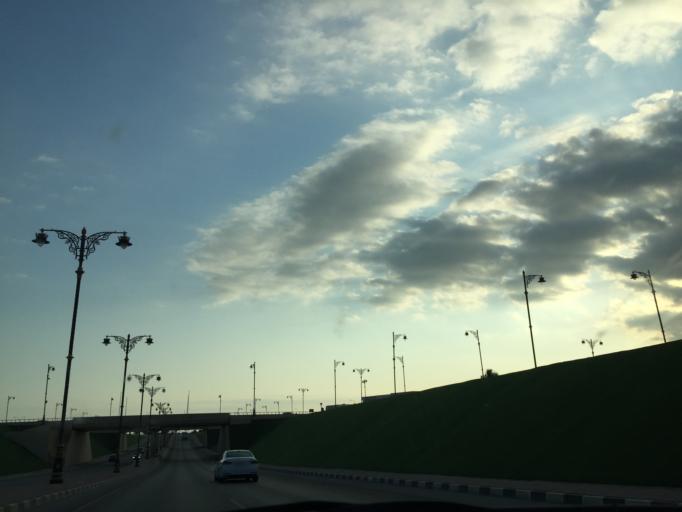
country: OM
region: Zufar
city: Salalah
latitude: 17.0343
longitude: 54.0598
